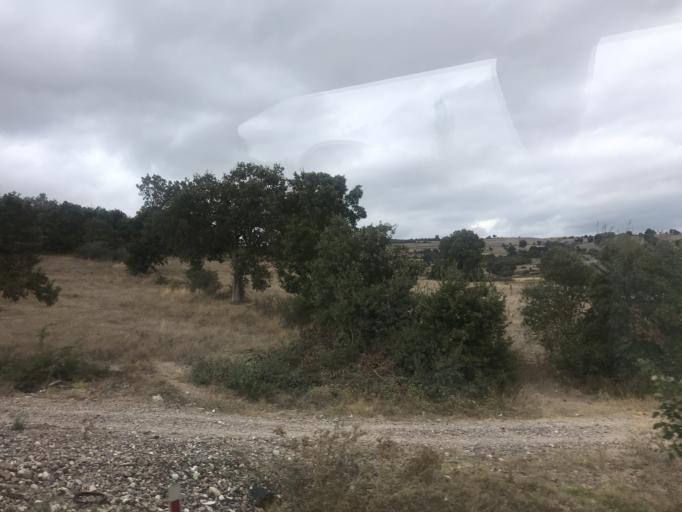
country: TR
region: Balikesir
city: Ertugrul
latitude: 39.6396
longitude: 27.7046
